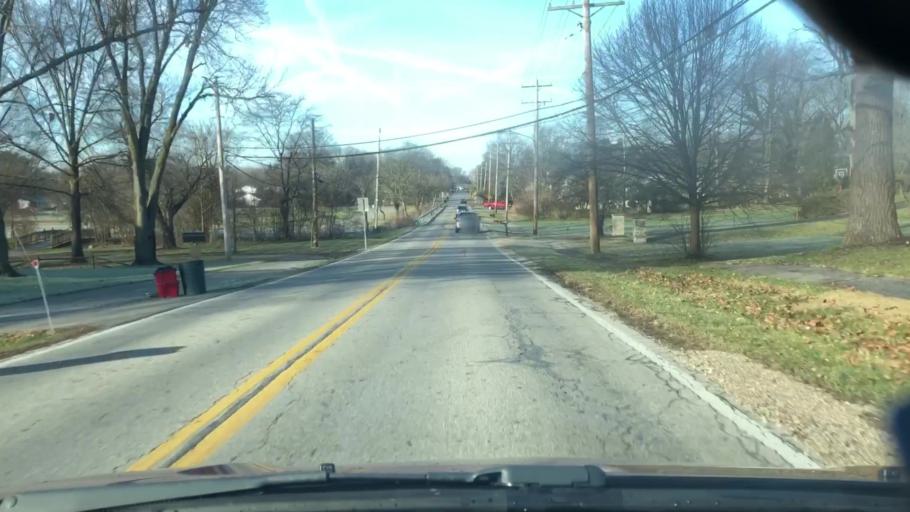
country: US
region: Ohio
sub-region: Franklin County
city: Westerville
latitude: 40.1196
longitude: -82.9091
